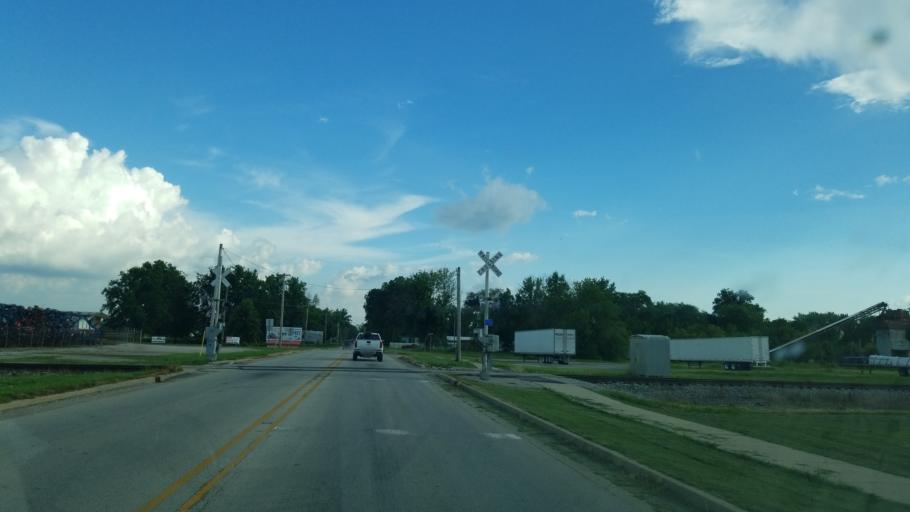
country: US
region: Illinois
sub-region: Marion County
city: Sandoval
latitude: 38.6139
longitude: -89.1145
